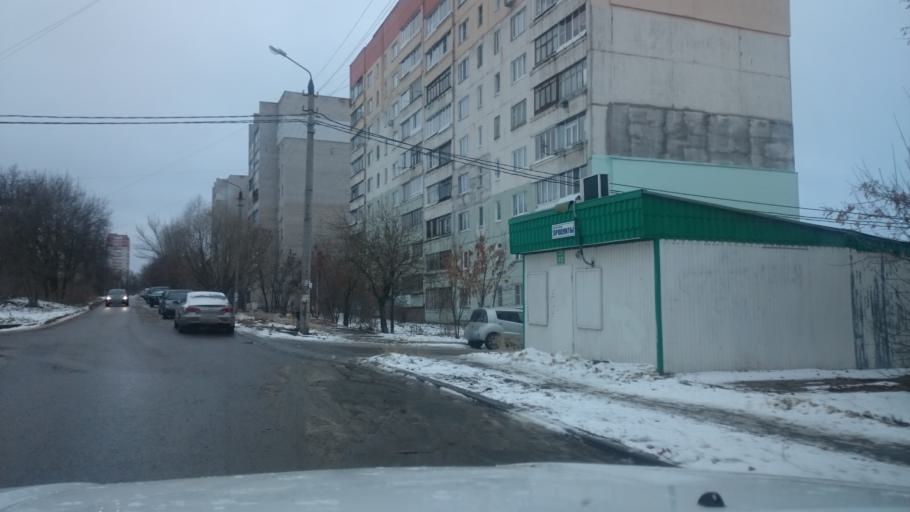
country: RU
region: Tula
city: Mendeleyevskiy
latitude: 54.1837
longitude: 37.5686
